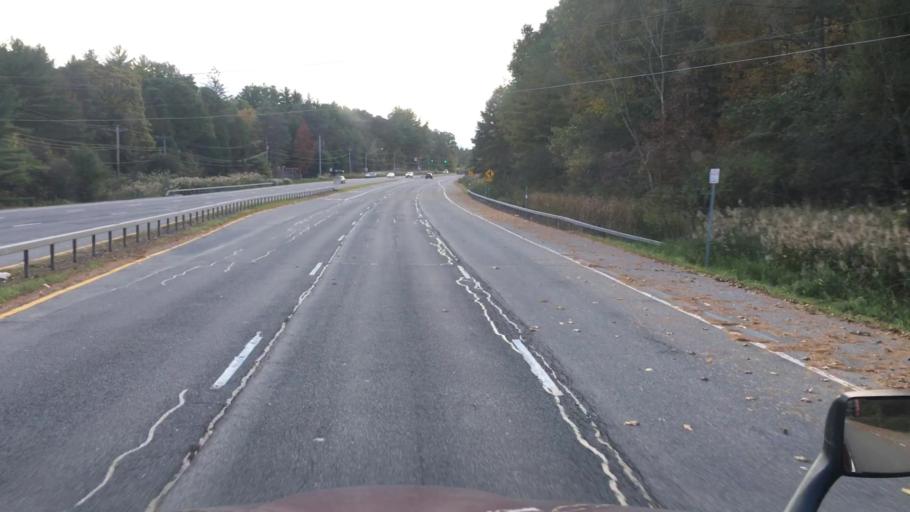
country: US
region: New York
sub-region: Saratoga County
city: Saratoga Springs
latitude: 43.0509
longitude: -73.8118
